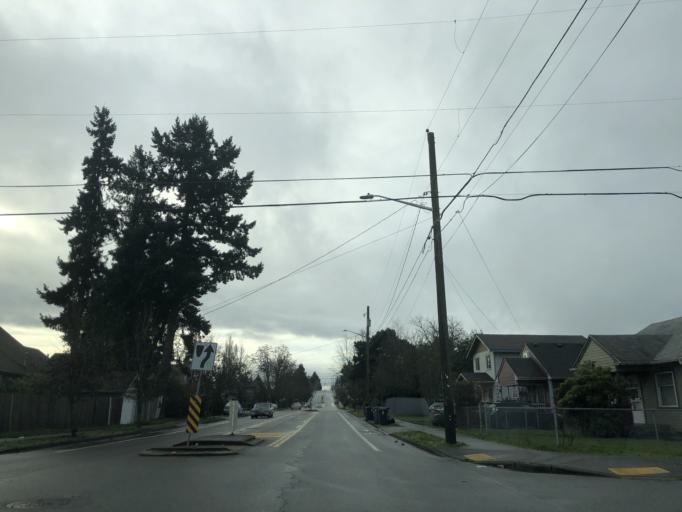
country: US
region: Washington
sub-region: Pierce County
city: Tacoma
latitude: 47.2176
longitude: -122.4582
